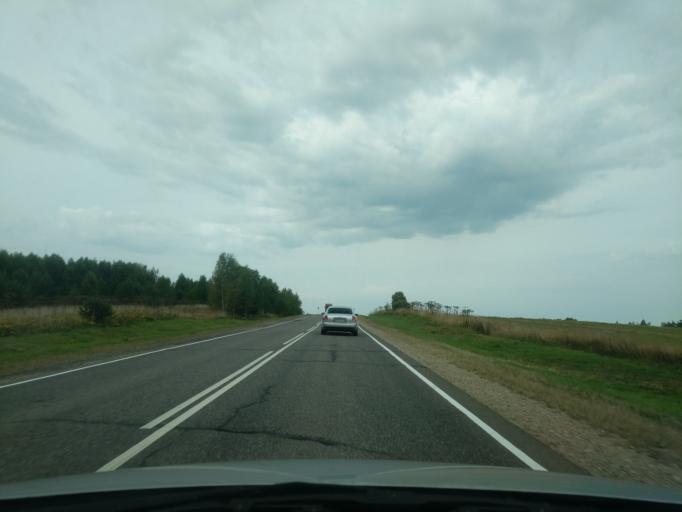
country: RU
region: Kirov
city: Mirnyy
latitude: 58.2731
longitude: 47.7754
